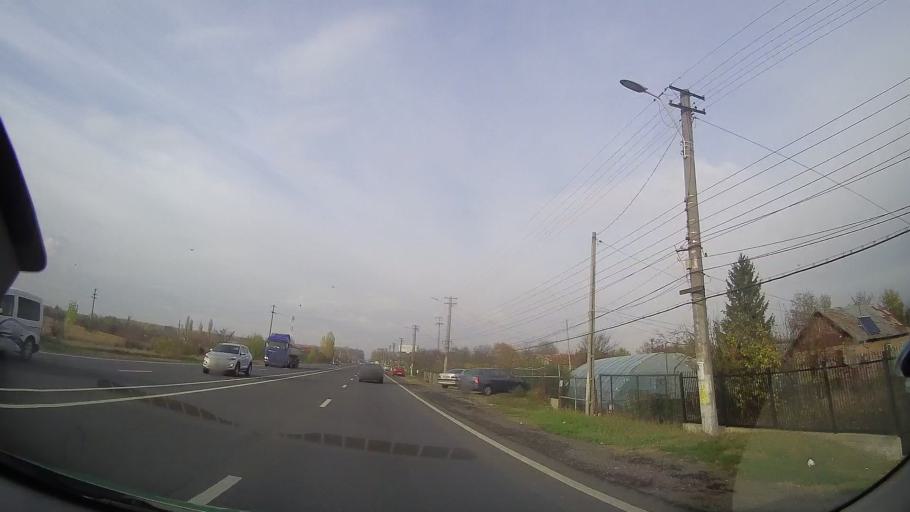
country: RO
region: Prahova
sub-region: Comuna Puchenii Mari
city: Puchenii Mari
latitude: 44.8182
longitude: 26.0817
